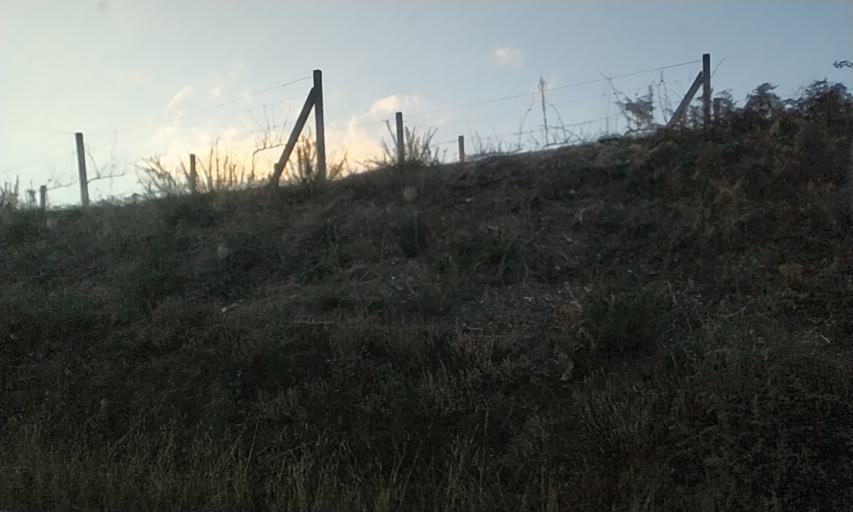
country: PT
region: Vila Real
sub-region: Mondim de Basto
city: Mondim de Basto
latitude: 41.4678
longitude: -7.9535
